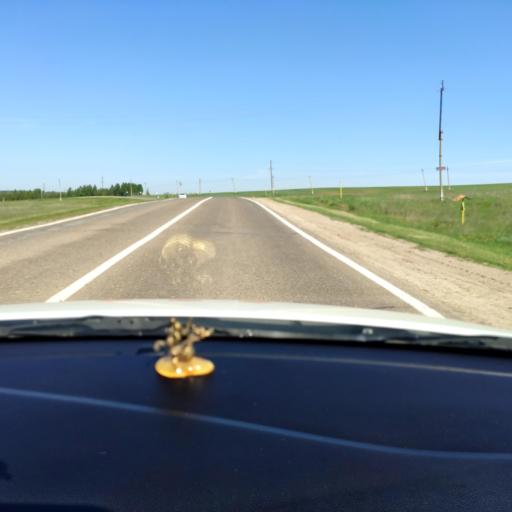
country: RU
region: Tatarstan
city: Vysokaya Gora
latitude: 56.0156
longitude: 49.2820
